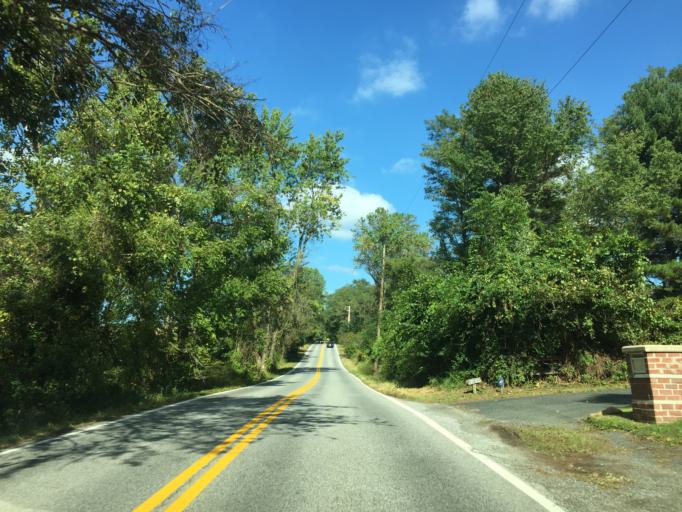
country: US
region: Maryland
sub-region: Harford County
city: Fallston
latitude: 39.4985
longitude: -76.4669
